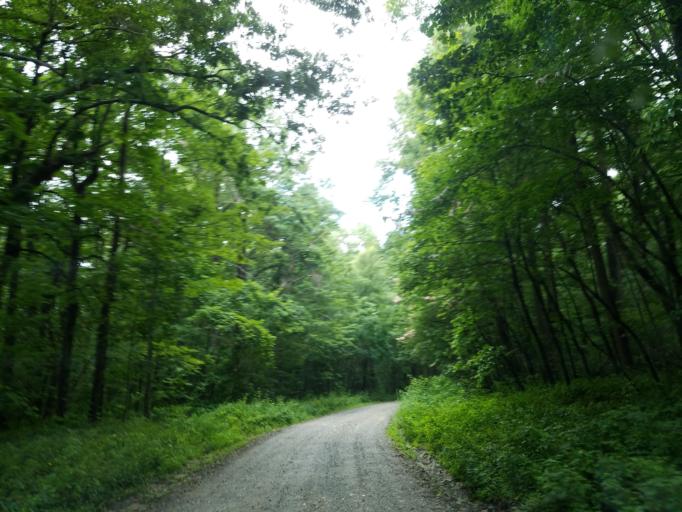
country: US
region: Georgia
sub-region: Lumpkin County
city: Dahlonega
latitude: 34.6401
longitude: -84.1612
